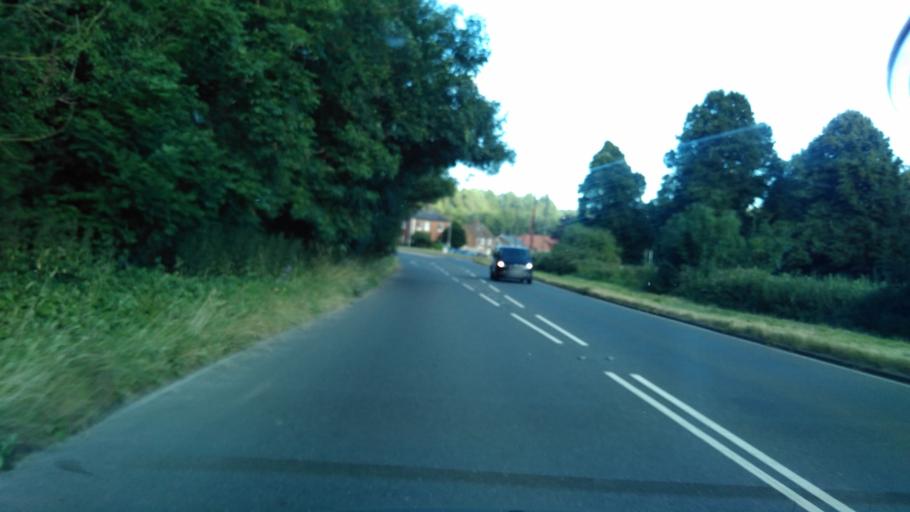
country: GB
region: England
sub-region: Kent
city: Dunkirk
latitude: 51.2452
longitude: 0.9698
